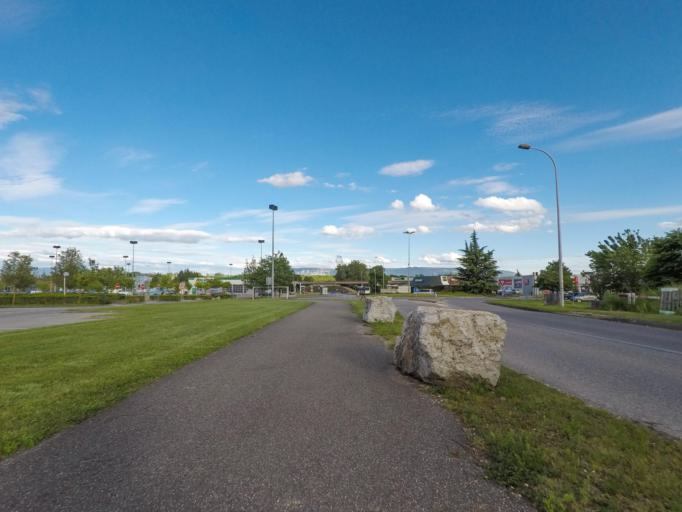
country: FR
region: Rhone-Alpes
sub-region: Departement de l'Ain
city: Thoiry
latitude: 46.2277
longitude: 5.9914
